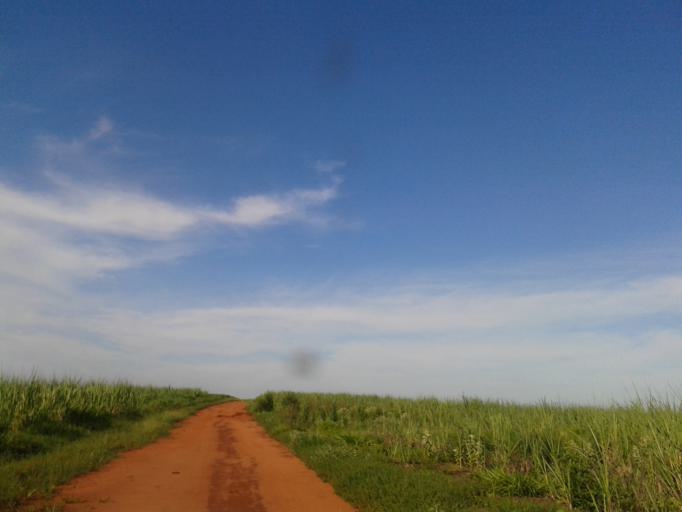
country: BR
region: Minas Gerais
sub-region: Santa Vitoria
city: Santa Vitoria
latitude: -19.0930
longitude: -49.9834
